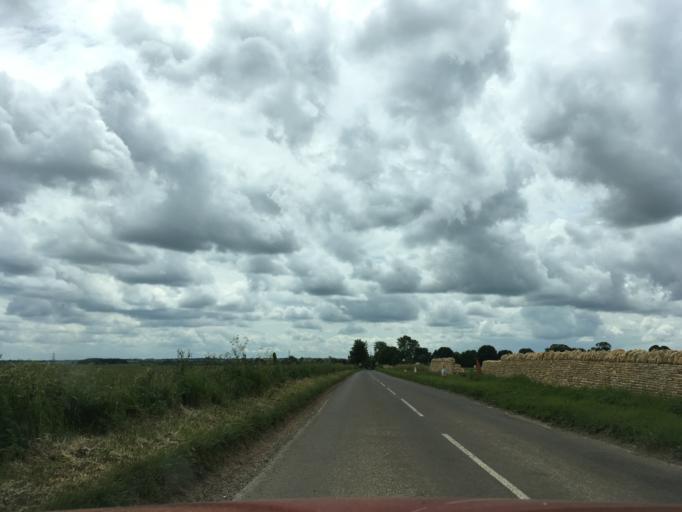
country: GB
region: England
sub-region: South Gloucestershire
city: Horton
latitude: 51.5147
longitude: -2.3336
